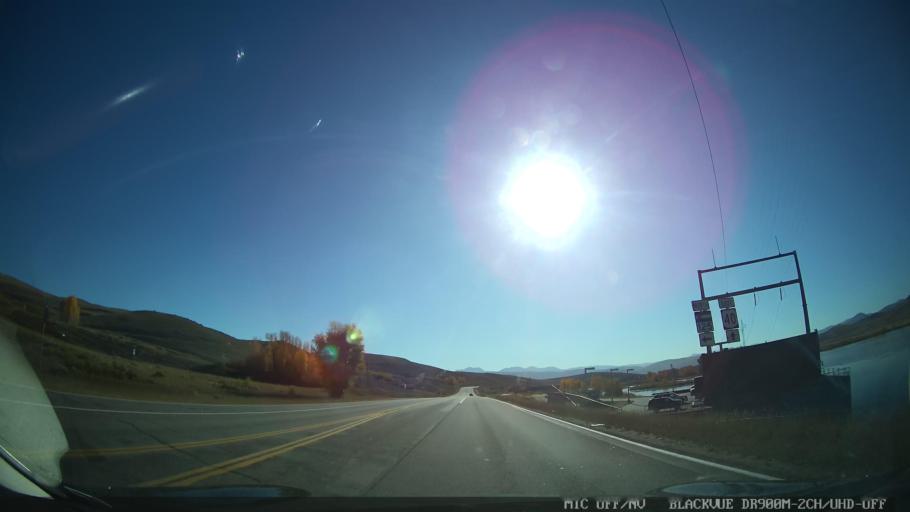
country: US
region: Colorado
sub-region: Grand County
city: Granby
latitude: 40.1093
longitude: -105.9838
